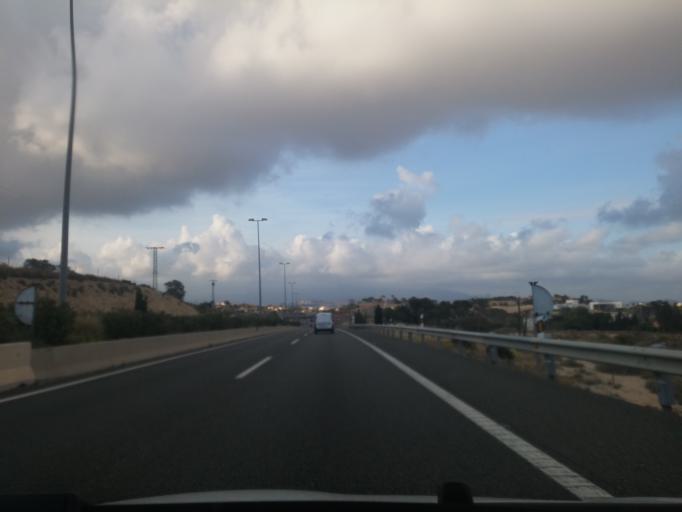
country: ES
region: Valencia
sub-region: Provincia de Alicante
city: San Juan de Alicante
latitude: 38.3938
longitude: -0.4511
